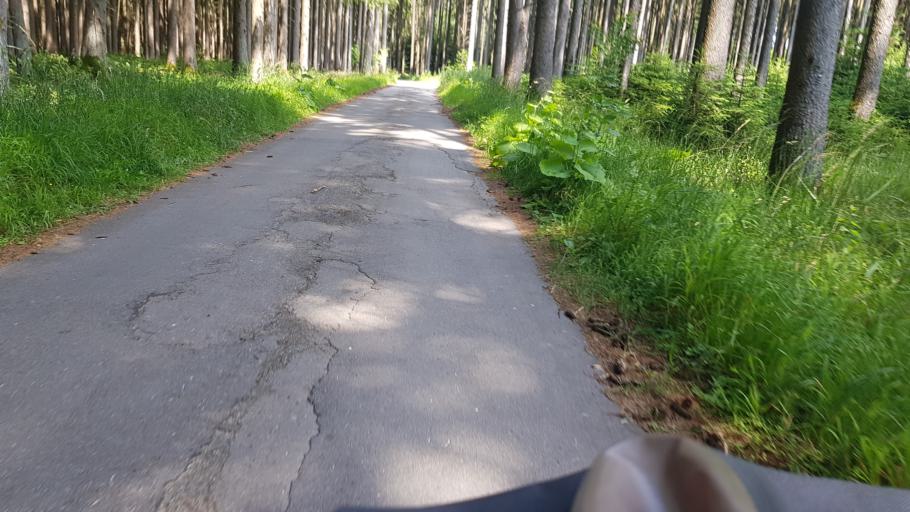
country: DE
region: Bavaria
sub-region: Upper Bavaria
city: Gauting
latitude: 48.0373
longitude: 11.3991
